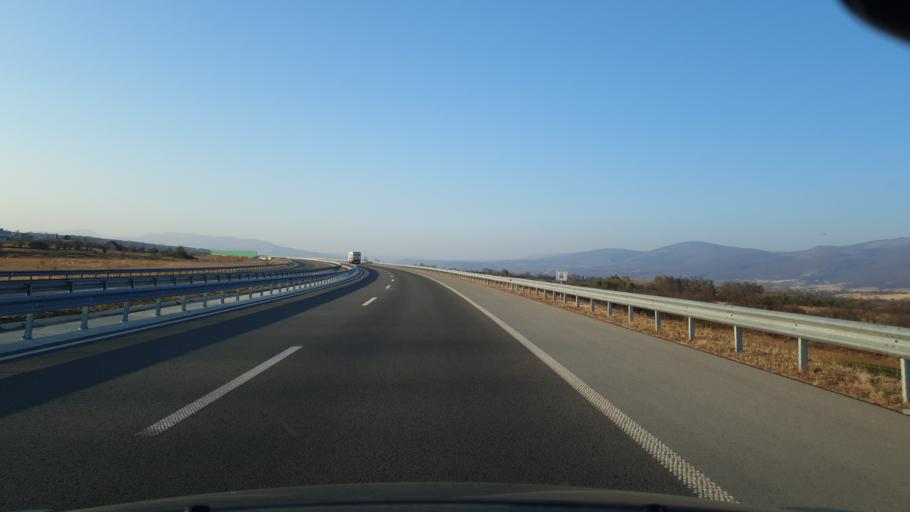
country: RS
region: Central Serbia
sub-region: Pirotski Okrug
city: Dimitrovgrad
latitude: 43.0691
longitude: 22.6779
